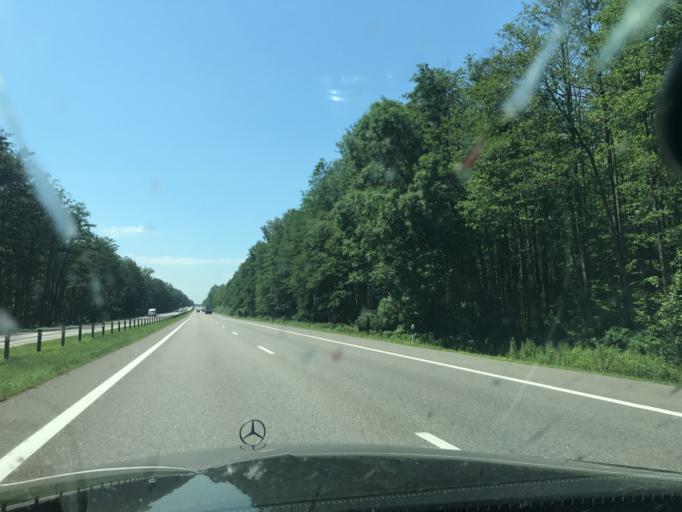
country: BY
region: Minsk
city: Enyerhyetykaw
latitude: 53.5760
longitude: 27.0125
